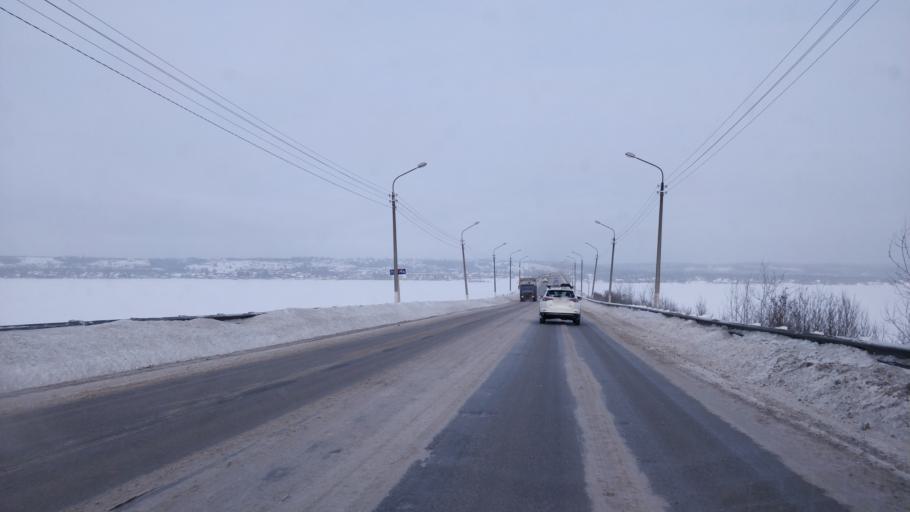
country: RU
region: Perm
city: Polazna
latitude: 58.1555
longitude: 56.4178
